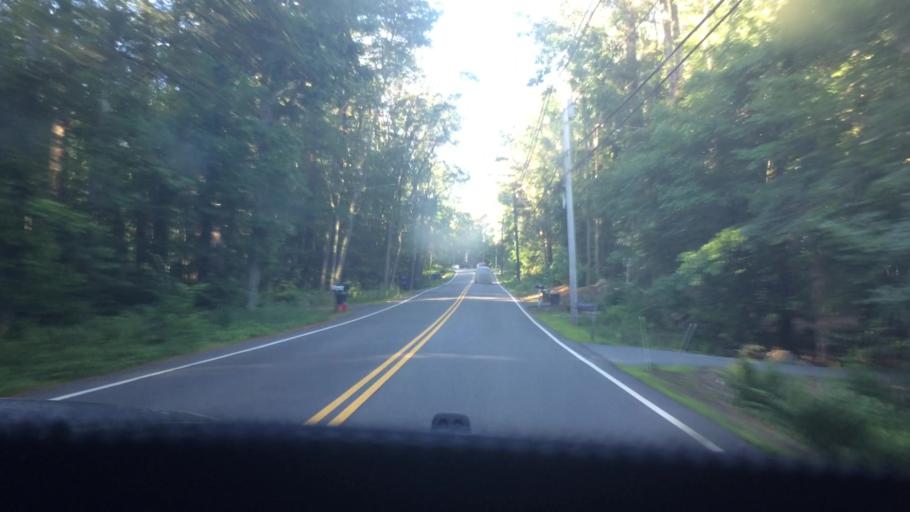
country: US
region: Massachusetts
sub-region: Essex County
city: Andover
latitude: 42.6294
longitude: -71.0922
